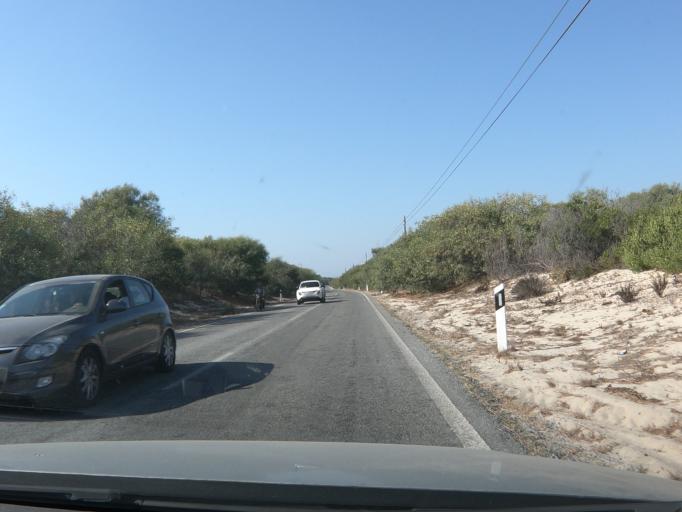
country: PT
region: Setubal
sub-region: Setubal
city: Setubal
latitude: 38.4077
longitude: -8.8108
